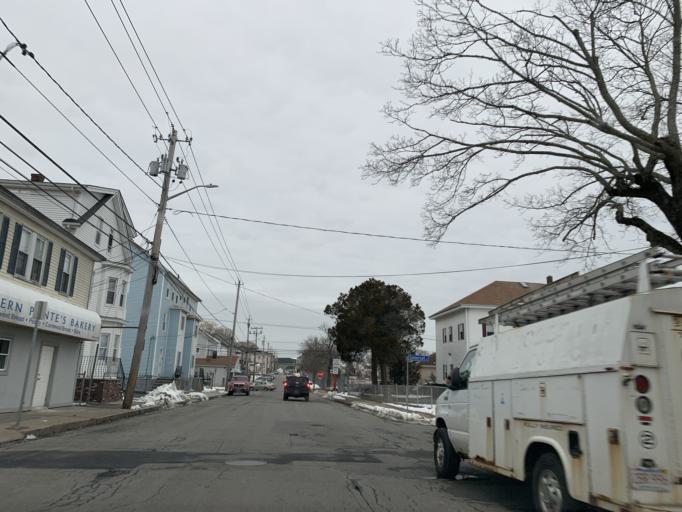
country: US
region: Massachusetts
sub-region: Bristol County
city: Fall River
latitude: 41.6862
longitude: -71.1488
